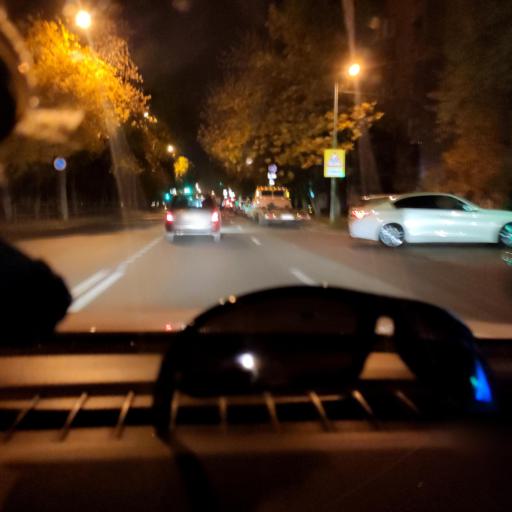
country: RU
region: Samara
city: Samara
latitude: 53.1963
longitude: 50.1692
